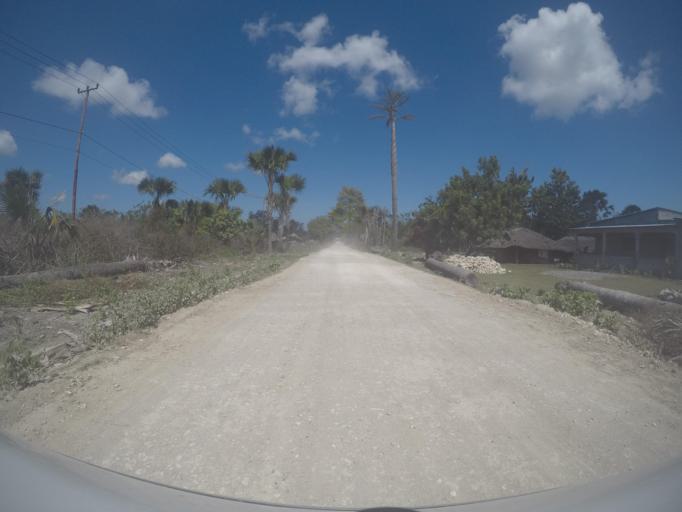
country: TL
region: Viqueque
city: Viqueque
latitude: -8.9253
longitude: 126.4046
